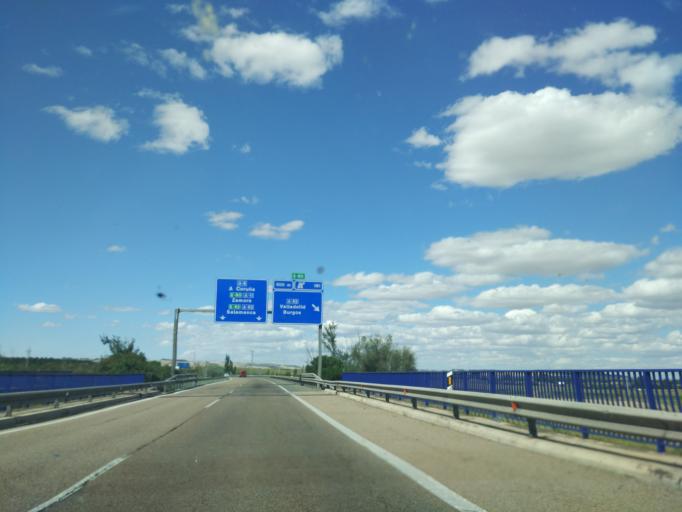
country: ES
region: Castille and Leon
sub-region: Provincia de Valladolid
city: Tordesillas
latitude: 41.4908
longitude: -4.9839
